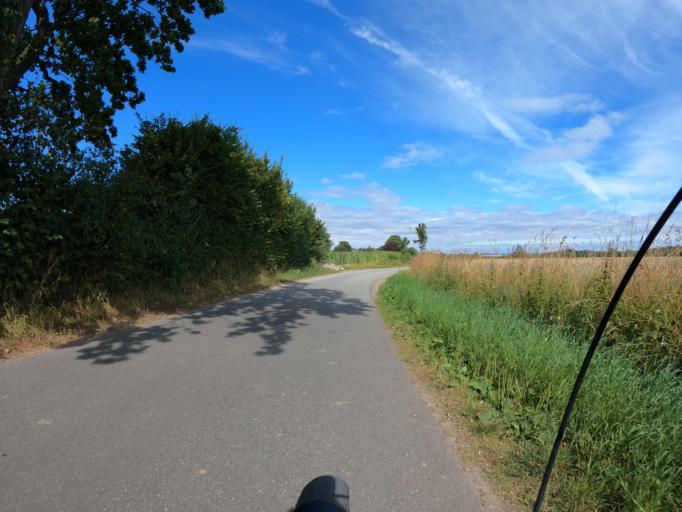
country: DE
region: Schleswig-Holstein
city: Steinbergkirche
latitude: 54.7799
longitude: 9.7605
